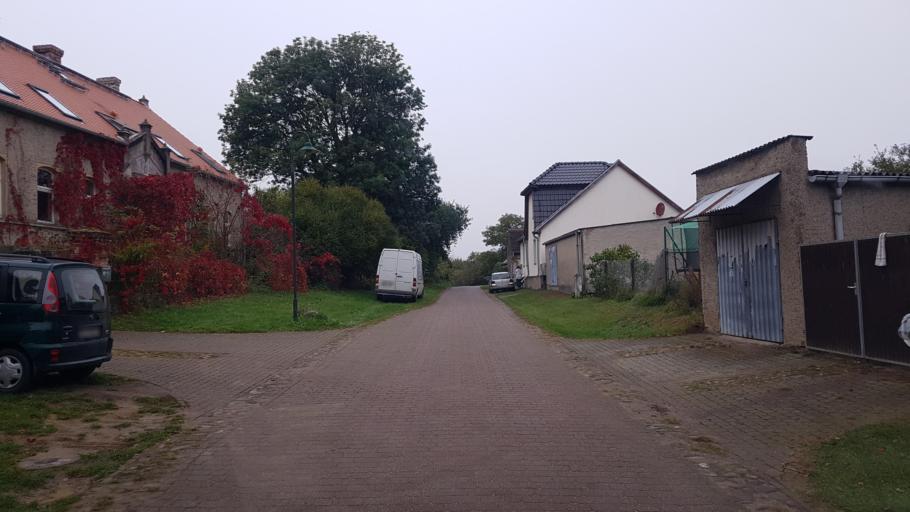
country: DE
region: Brandenburg
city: Furstenwalde
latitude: 52.4337
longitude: 14.0134
